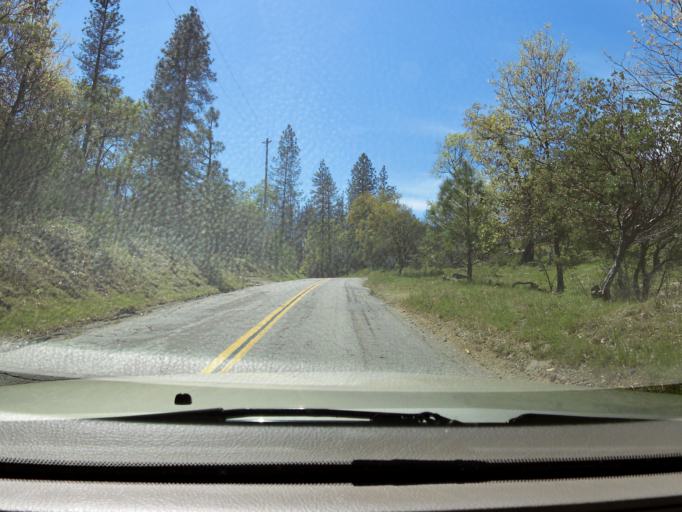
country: US
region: California
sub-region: Madera County
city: Oakhurst
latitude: 37.2455
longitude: -119.5192
